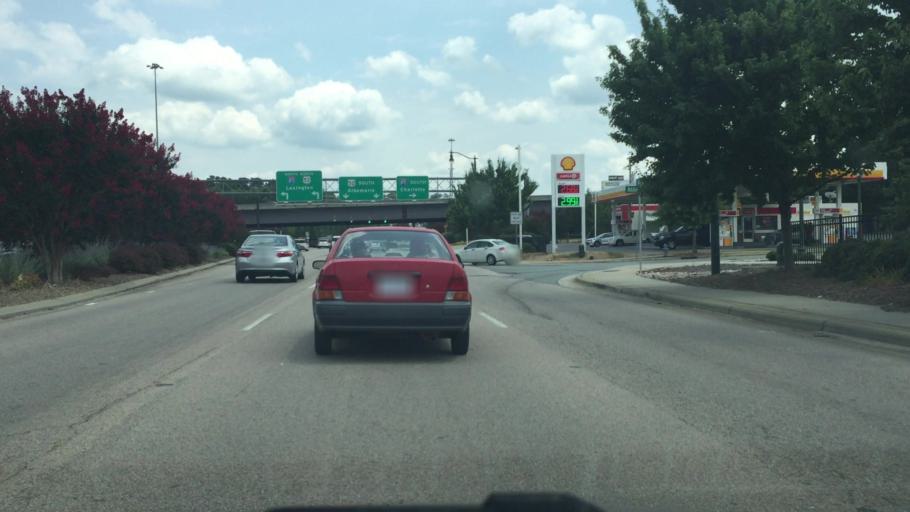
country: US
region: North Carolina
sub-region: Rowan County
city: Salisbury
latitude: 35.6591
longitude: -80.4611
